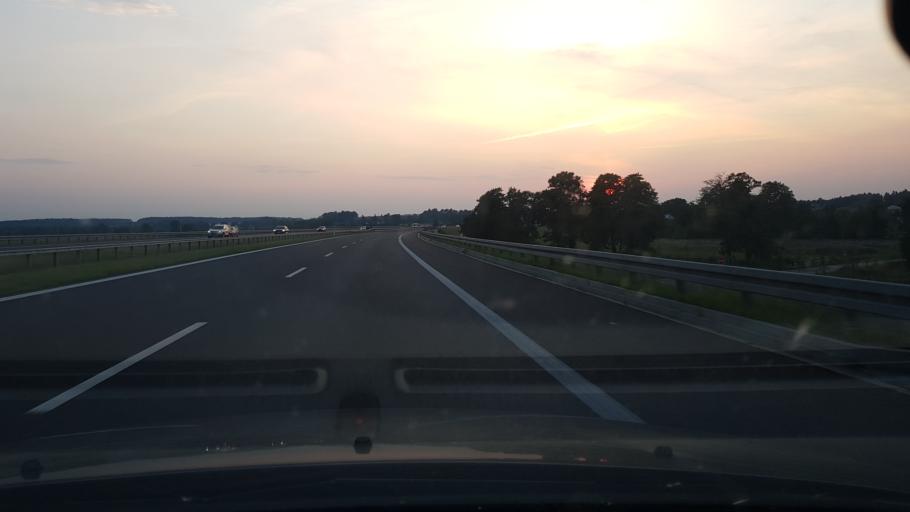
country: PL
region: Warmian-Masurian Voivodeship
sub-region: Powiat nidzicki
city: Nidzica
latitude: 53.3405
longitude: 20.4111
